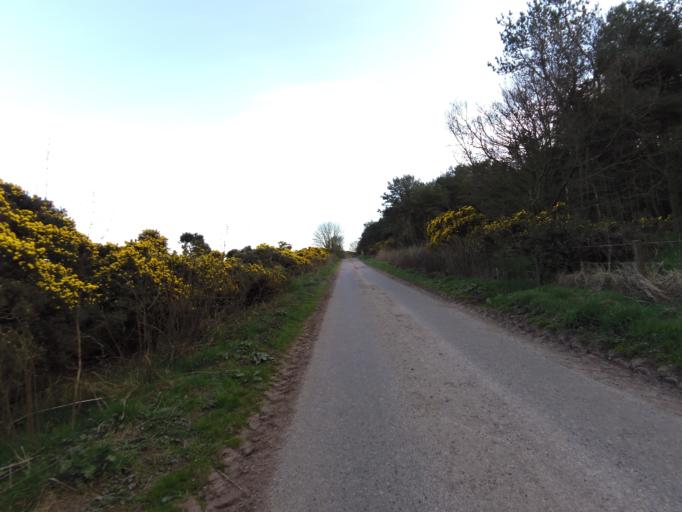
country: GB
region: Scotland
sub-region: Aberdeenshire
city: Stonehaven
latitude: 56.9251
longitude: -2.2285
